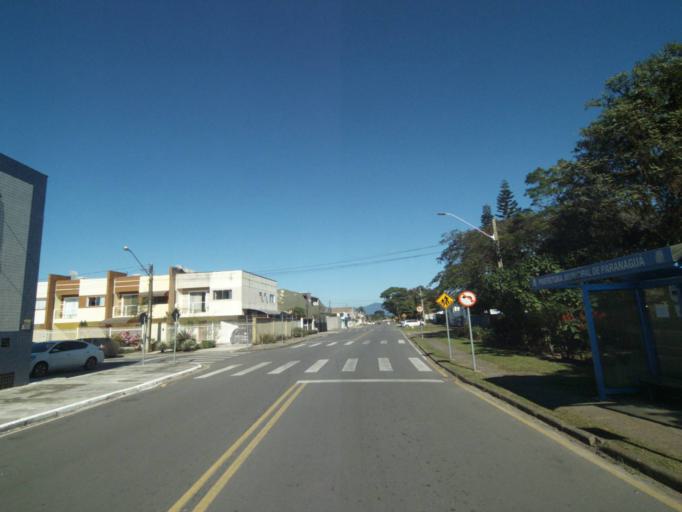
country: BR
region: Parana
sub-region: Paranagua
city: Paranagua
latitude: -25.5305
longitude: -48.5269
